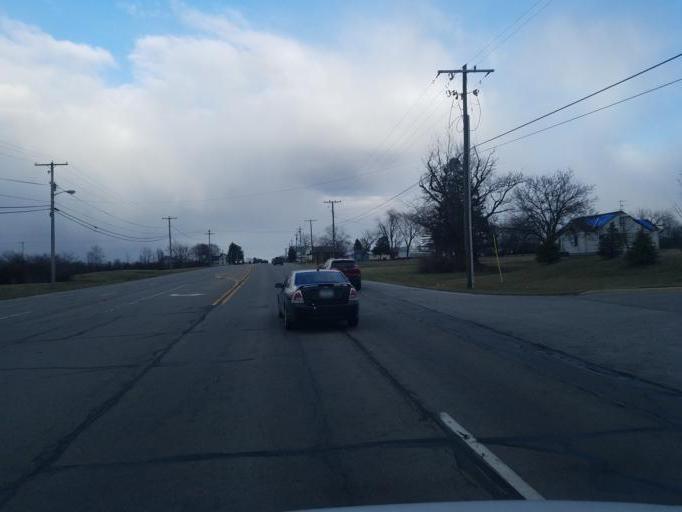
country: US
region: Indiana
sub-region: Marion County
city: Cumberland
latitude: 39.7773
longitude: -85.9403
